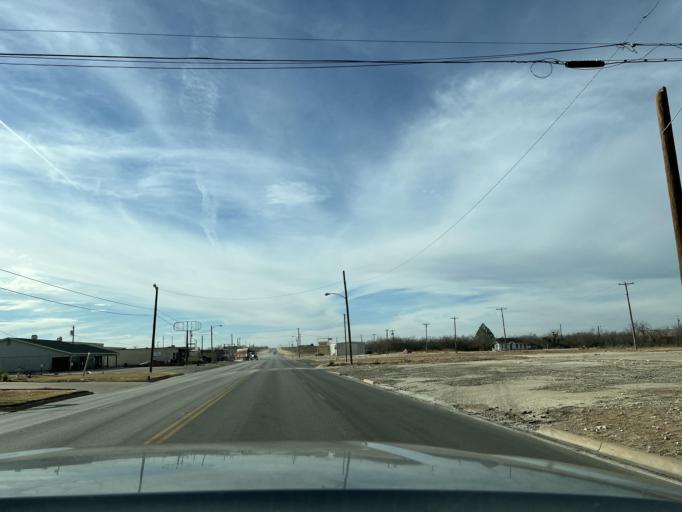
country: US
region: Texas
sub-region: Jones County
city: Anson
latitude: 32.7516
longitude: -99.9020
